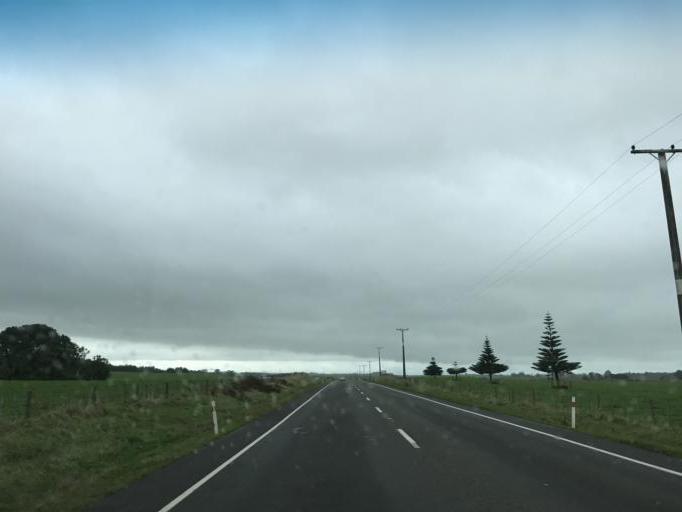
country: NZ
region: Manawatu-Wanganui
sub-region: Wanganui District
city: Wanganui
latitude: -39.8150
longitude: 174.8124
